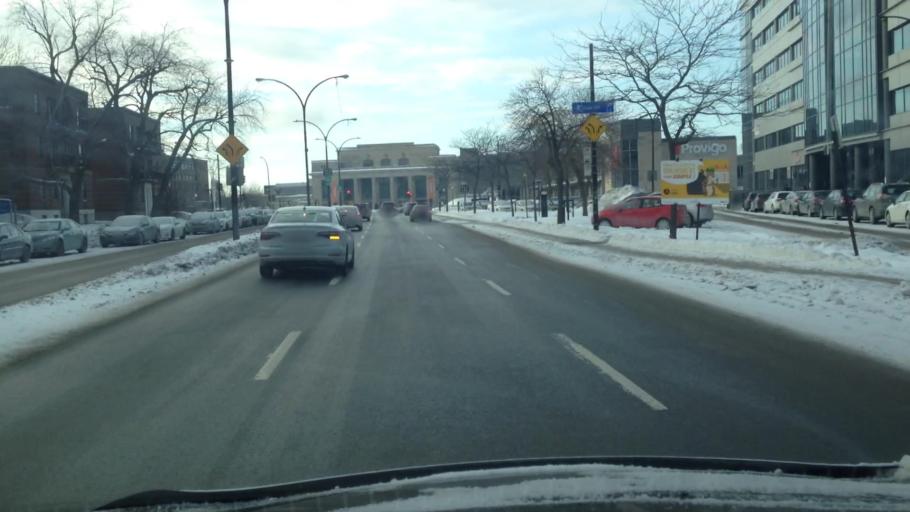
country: CA
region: Quebec
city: Mont-Royal
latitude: 45.5298
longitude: -73.6205
